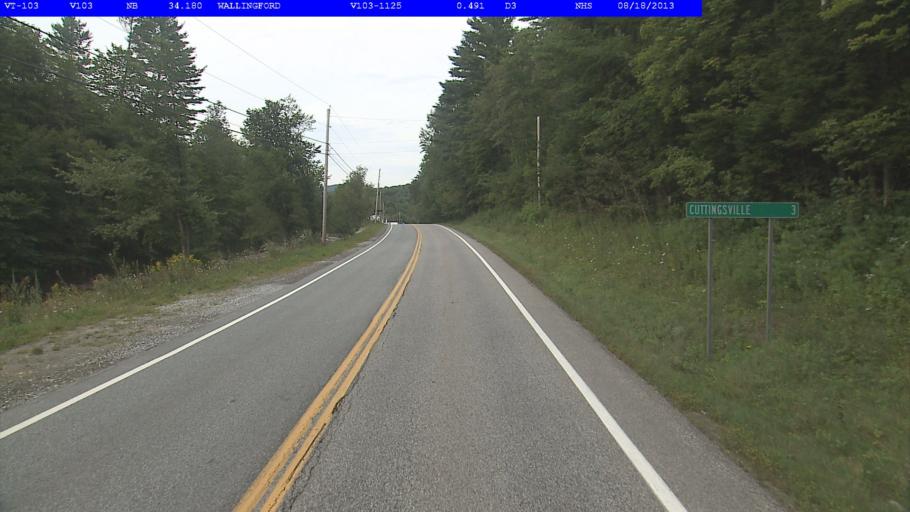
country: US
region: Vermont
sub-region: Rutland County
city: Rutland
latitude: 43.4538
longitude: -72.8784
